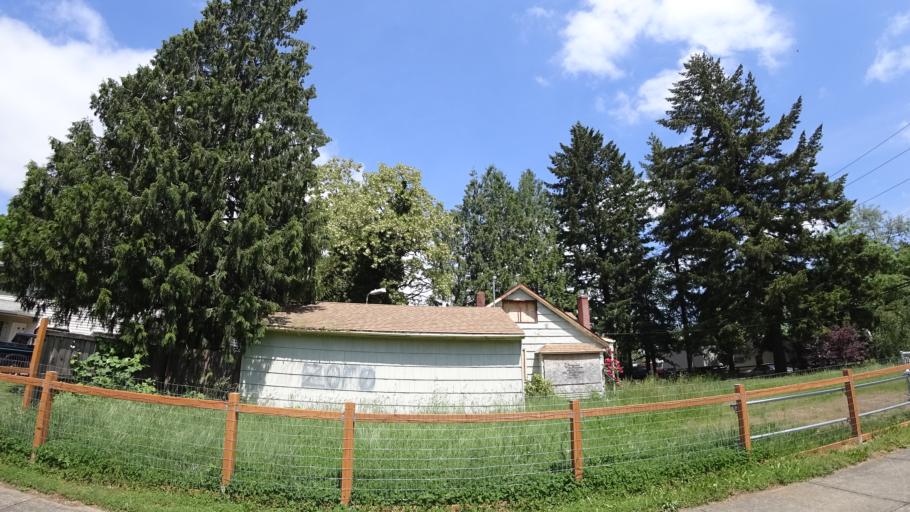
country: US
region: Oregon
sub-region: Multnomah County
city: Gresham
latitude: 45.5031
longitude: -122.4852
